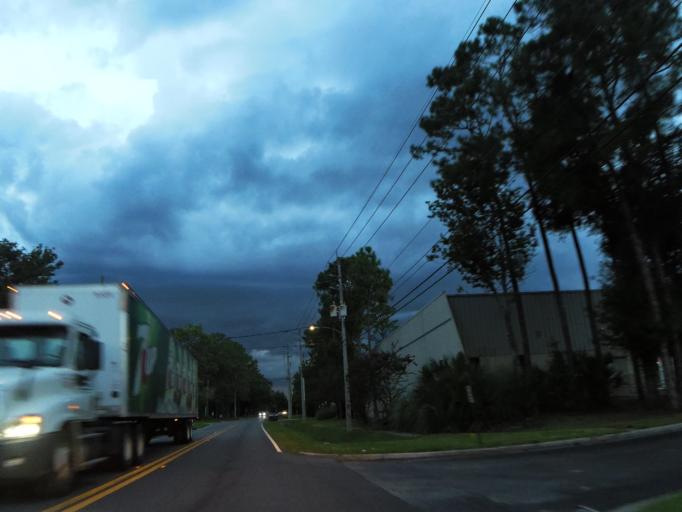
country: US
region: Florida
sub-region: Duval County
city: Jacksonville
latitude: 30.2618
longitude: -81.6101
